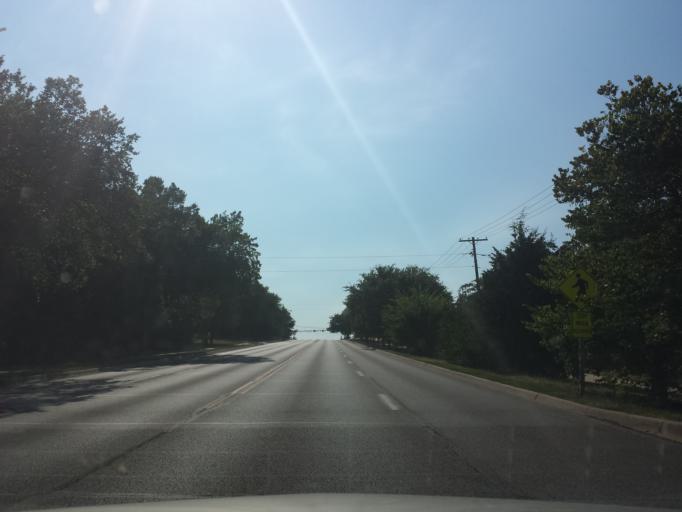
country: US
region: Kansas
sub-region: Riley County
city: Manhattan
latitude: 39.2036
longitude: -96.6232
